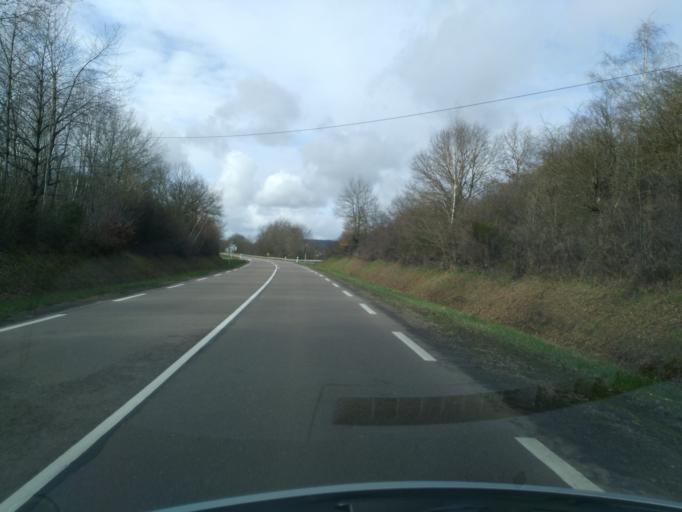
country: FR
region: Bourgogne
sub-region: Departement de Saone-et-Loire
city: Torcy
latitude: 46.7724
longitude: 4.4289
